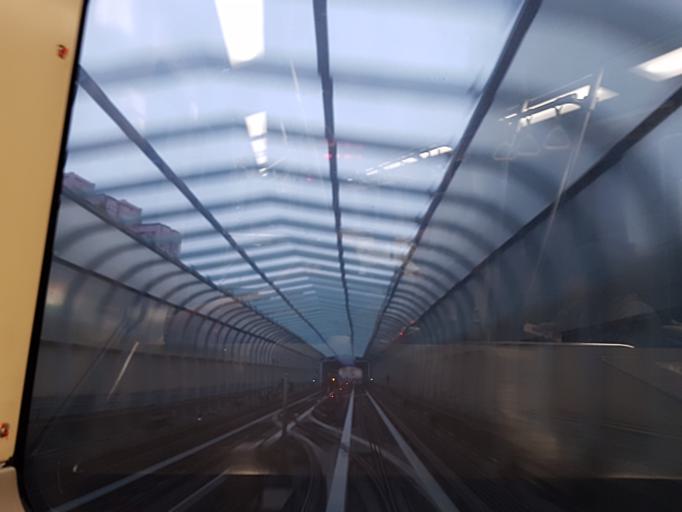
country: TW
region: Taipei
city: Taipei
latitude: 25.0723
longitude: 121.6081
